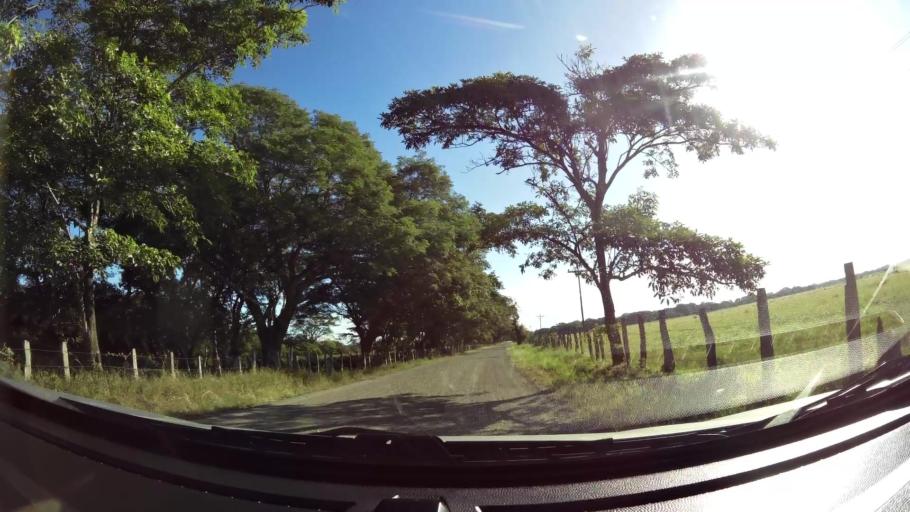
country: CR
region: Guanacaste
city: Sardinal
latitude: 10.4846
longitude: -85.5880
